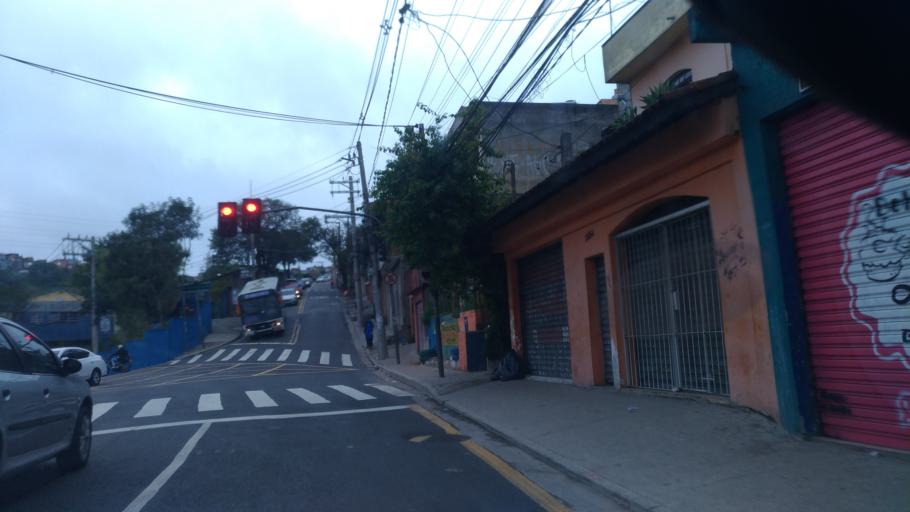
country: BR
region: Sao Paulo
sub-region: Sao Bernardo Do Campo
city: Sao Bernardo do Campo
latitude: -23.7079
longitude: -46.5228
